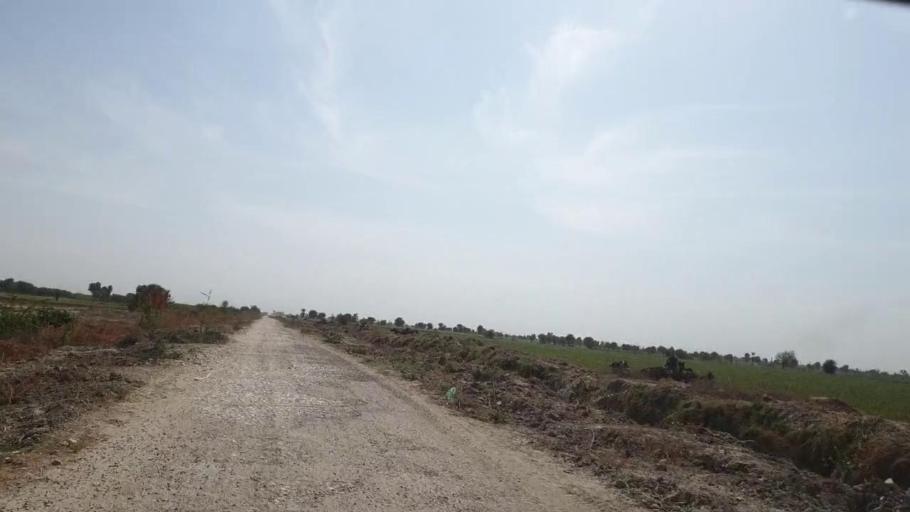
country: PK
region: Sindh
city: Nabisar
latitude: 25.0952
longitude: 69.5818
